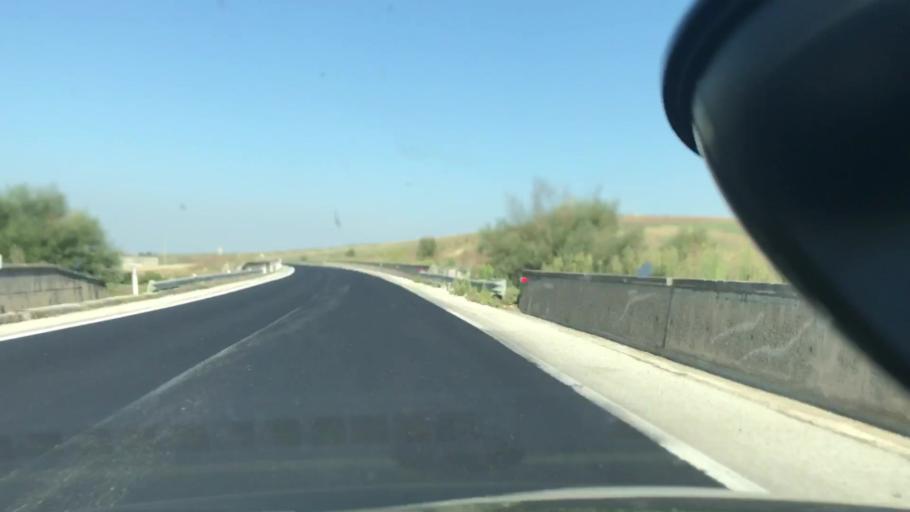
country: IT
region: Apulia
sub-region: Provincia di Barletta - Andria - Trani
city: Spinazzola
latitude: 40.9203
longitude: 16.0975
